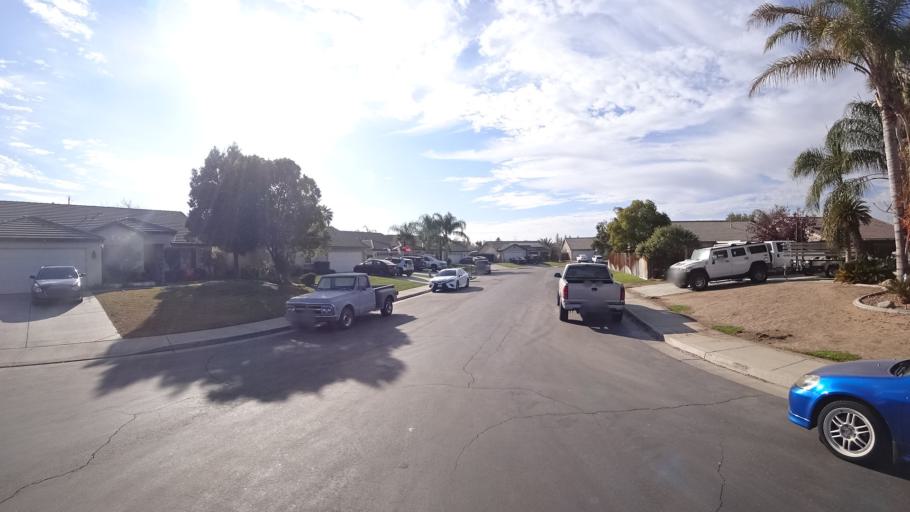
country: US
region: California
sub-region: Kern County
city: Greenacres
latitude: 35.3995
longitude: -119.1125
